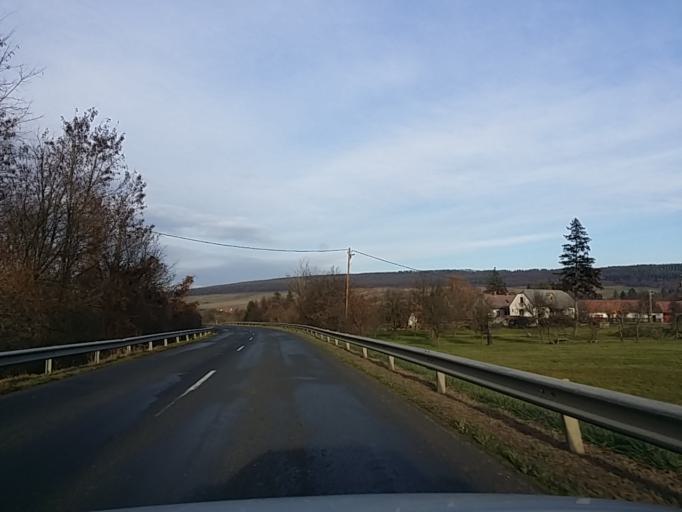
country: HU
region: Veszprem
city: Zanka
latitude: 46.9622
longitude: 17.6228
